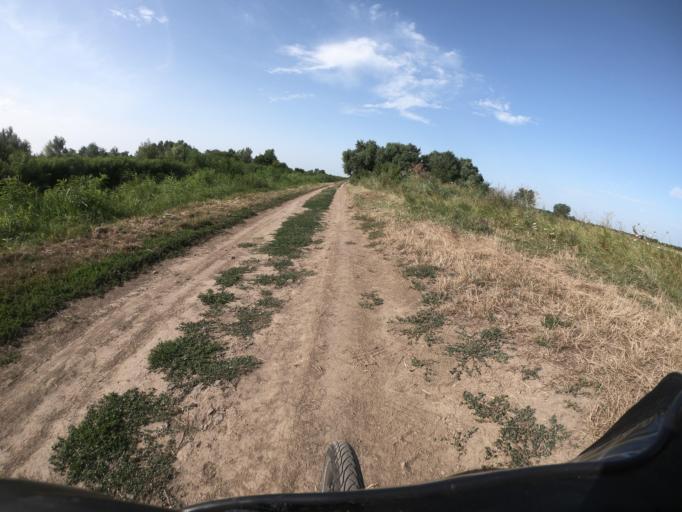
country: HU
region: Hajdu-Bihar
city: Tiszacsege
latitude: 47.6066
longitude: 20.9974
